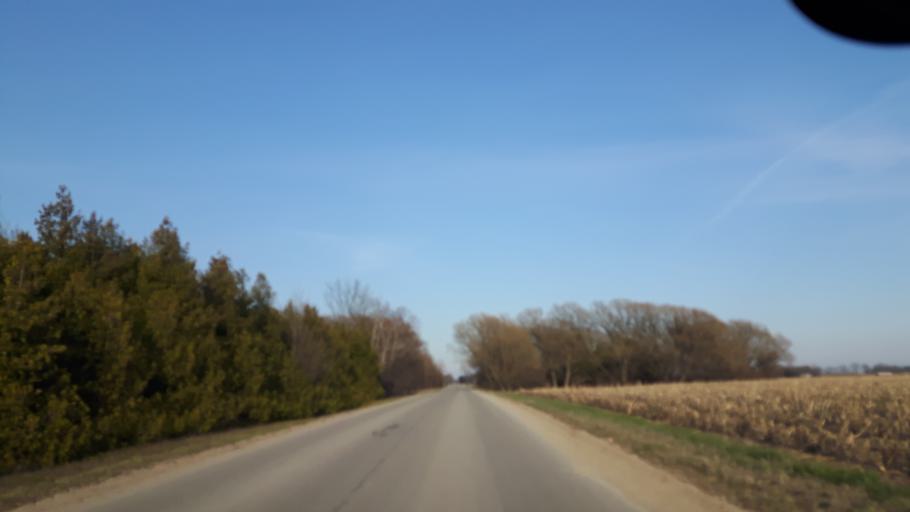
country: CA
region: Ontario
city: Goderich
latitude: 43.6983
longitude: -81.7001
